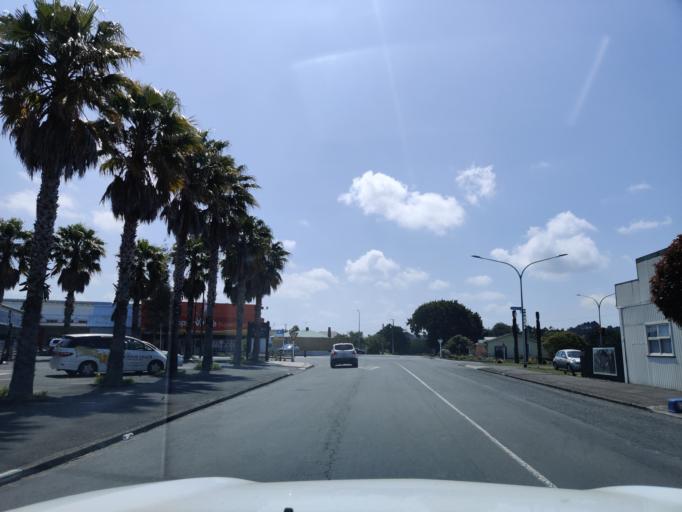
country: NZ
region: Auckland
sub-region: Auckland
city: Pukekohe East
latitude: -37.2576
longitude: 174.9477
